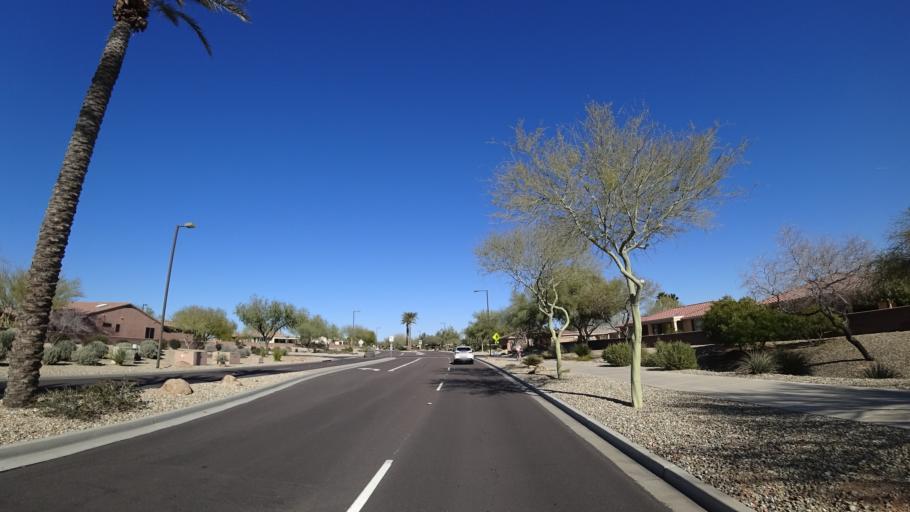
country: US
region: Arizona
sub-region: Maricopa County
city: Sun City West
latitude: 33.6676
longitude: -112.4225
